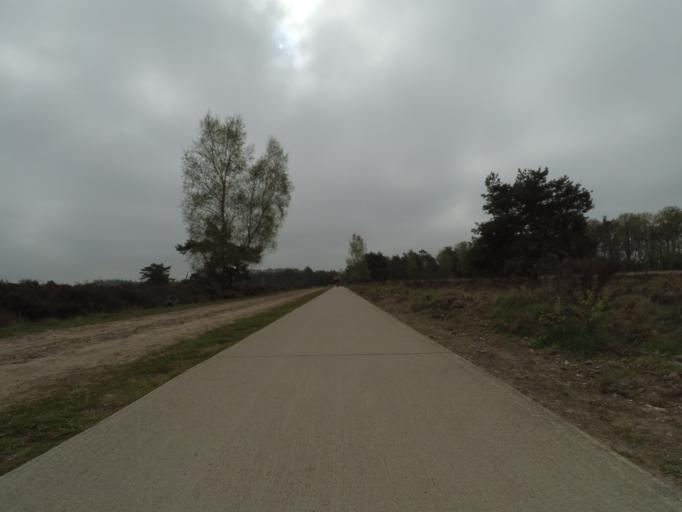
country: NL
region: Gelderland
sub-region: Gemeente Epe
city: Vaassen
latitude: 52.3177
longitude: 5.8950
